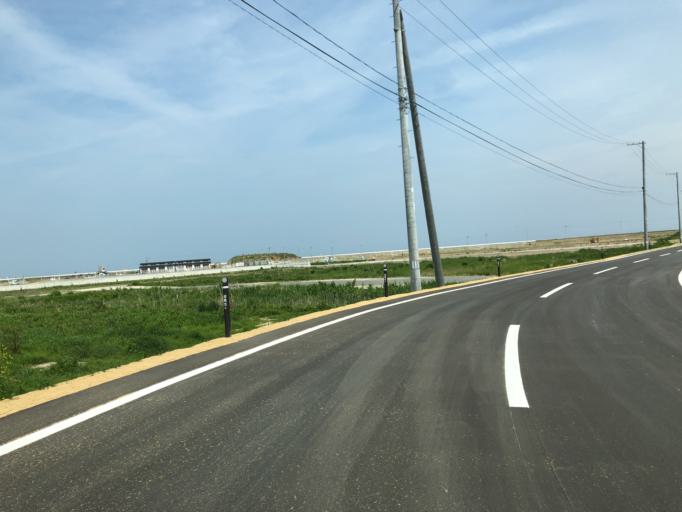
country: JP
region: Miyagi
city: Marumori
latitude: 37.7786
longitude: 140.9781
